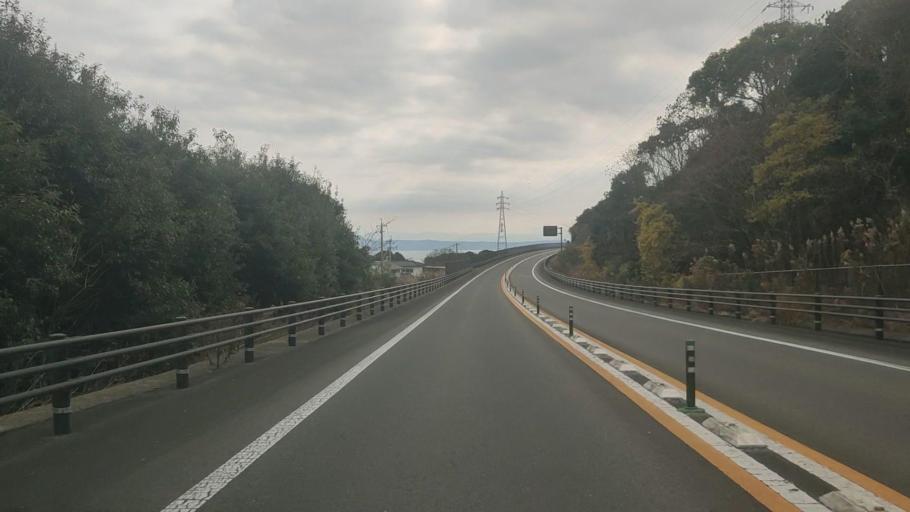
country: JP
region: Nagasaki
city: Shimabara
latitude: 32.7841
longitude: 130.3521
